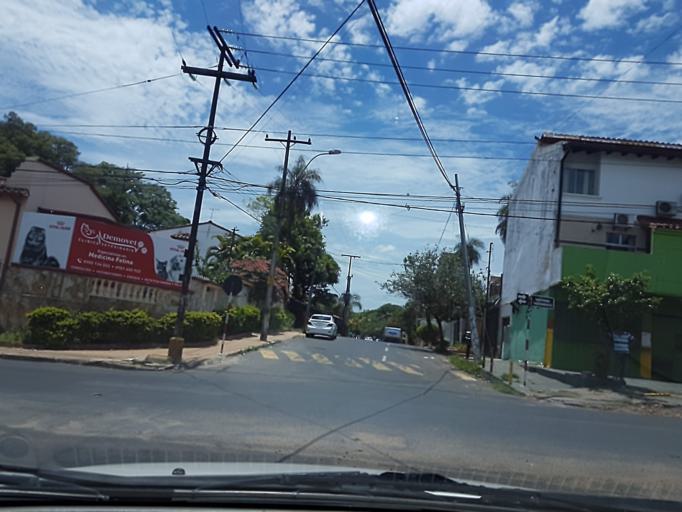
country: PY
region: Asuncion
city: Asuncion
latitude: -25.2580
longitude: -57.5794
